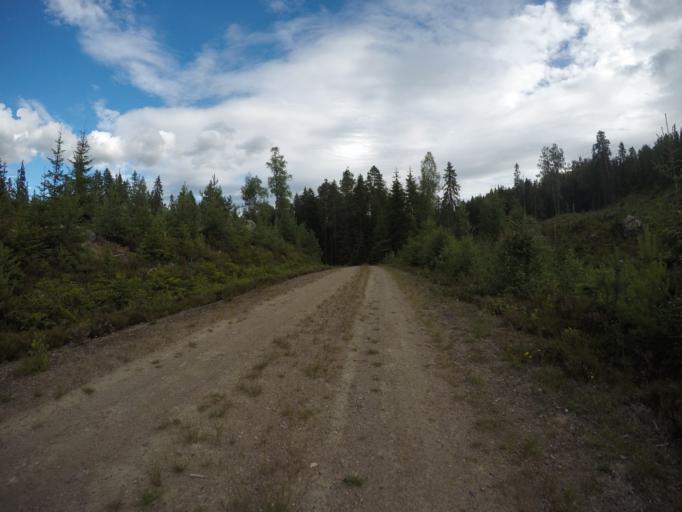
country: SE
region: Vaermland
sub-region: Filipstads Kommun
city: Lesjofors
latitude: 60.0321
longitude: 14.3763
